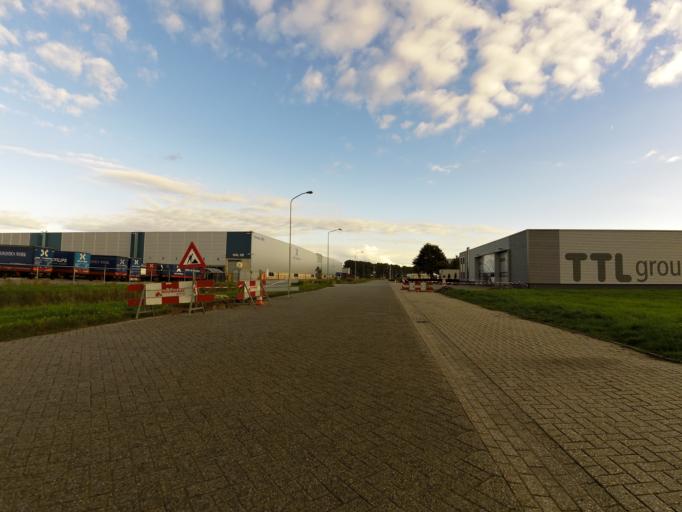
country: NL
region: Gelderland
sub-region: Gemeente Montferland
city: s-Heerenberg
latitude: 51.8768
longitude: 6.2664
